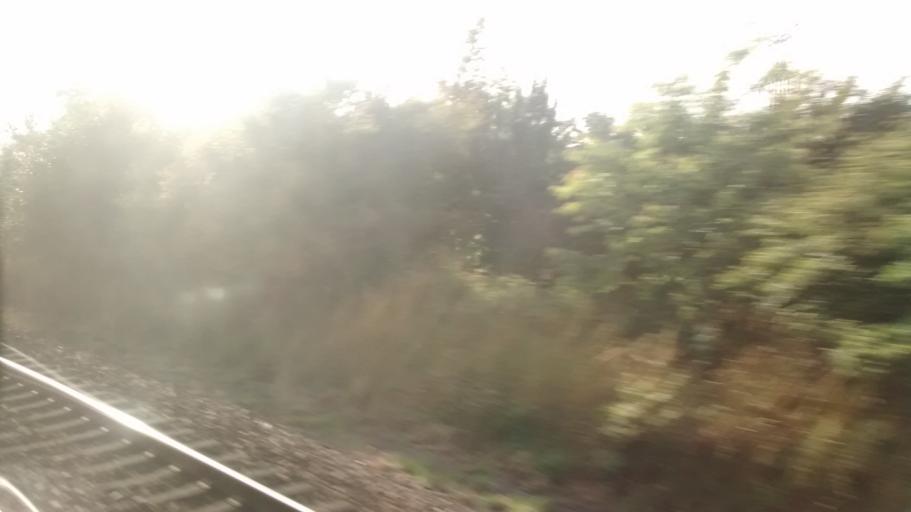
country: FR
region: Brittany
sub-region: Departement d'Ille-et-Vilaine
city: Servon-sur-Vilaine
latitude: 48.1055
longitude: -1.4318
